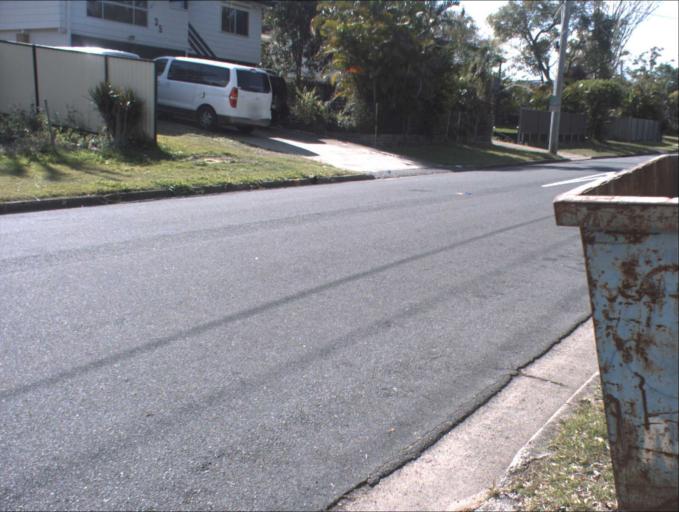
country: AU
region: Queensland
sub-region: Logan
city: Park Ridge South
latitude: -27.6900
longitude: 153.0112
